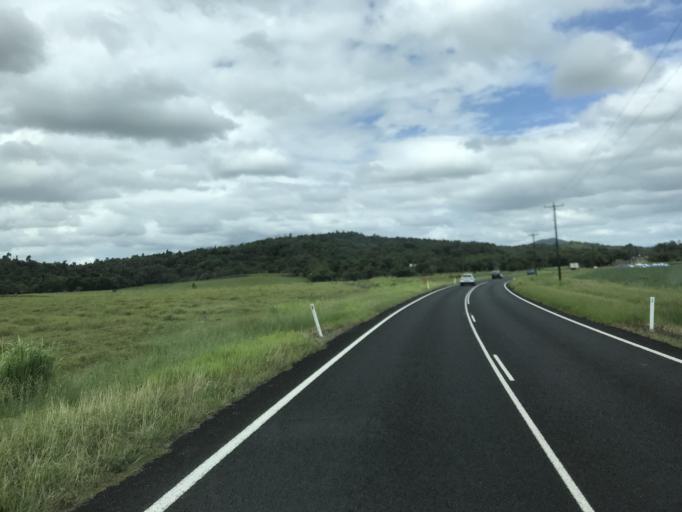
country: AU
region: Queensland
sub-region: Cassowary Coast
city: Innisfail
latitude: -17.8252
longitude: 146.0481
